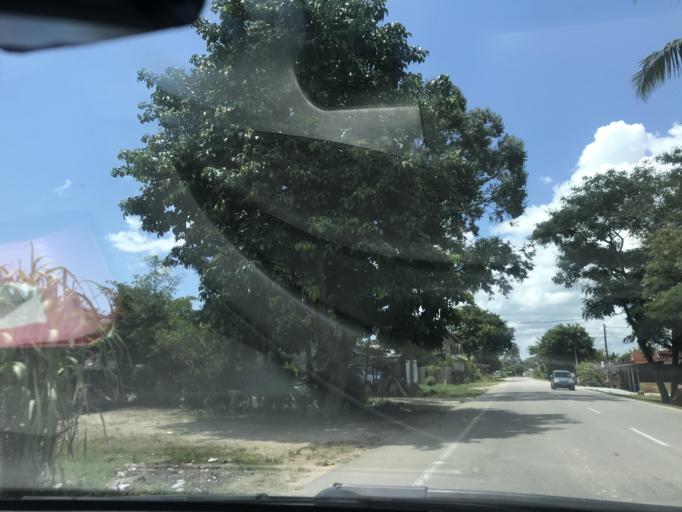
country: MY
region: Kelantan
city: Tumpat
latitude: 6.1997
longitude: 102.1269
